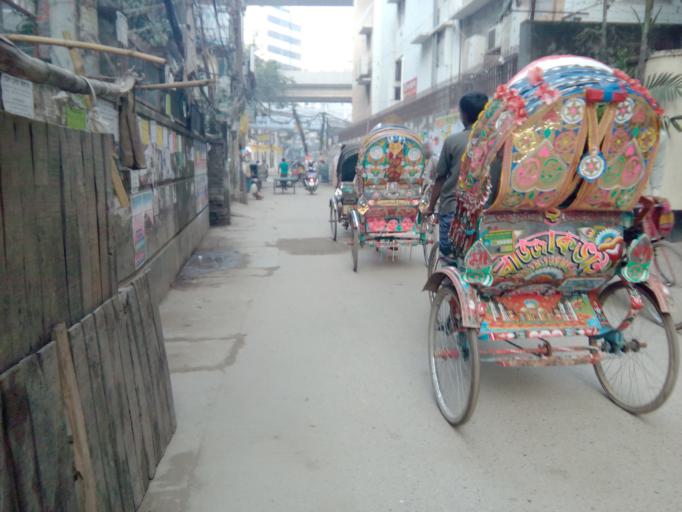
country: BD
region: Dhaka
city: Paltan
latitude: 23.7458
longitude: 90.4131
